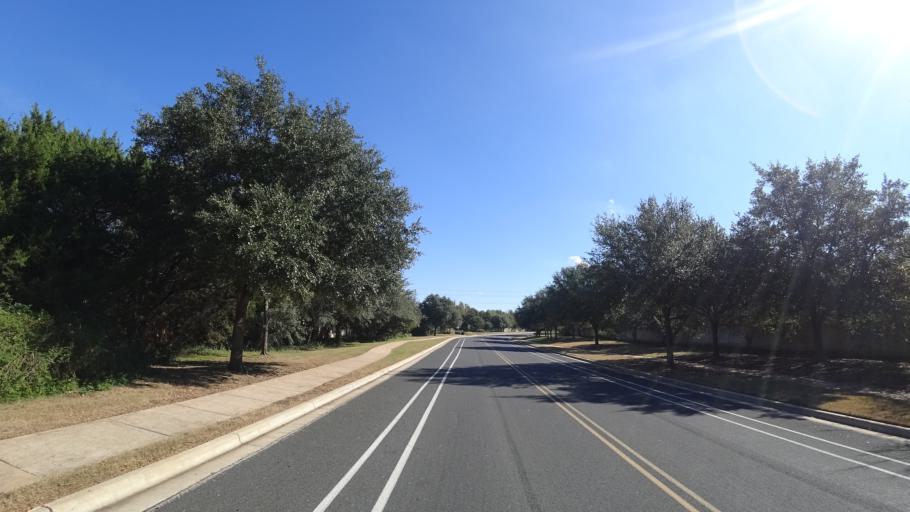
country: US
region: Texas
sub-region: Travis County
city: Hudson Bend
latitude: 30.3763
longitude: -97.9004
